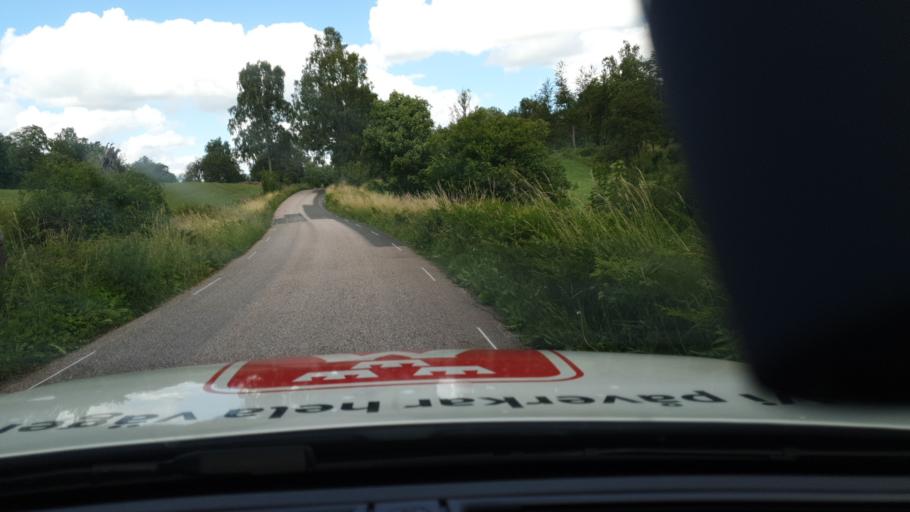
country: SE
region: Vaestra Goetaland
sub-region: Skovde Kommun
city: Stopen
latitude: 58.4638
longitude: 13.7408
